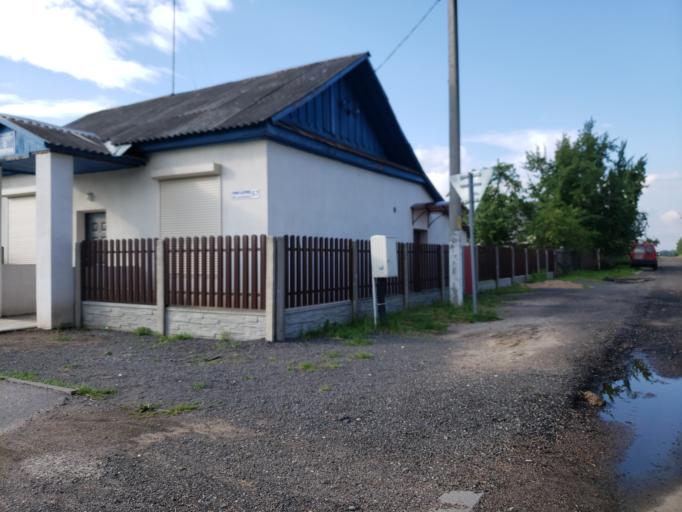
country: BY
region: Minsk
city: Chervyen'
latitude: 53.7038
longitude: 28.4390
